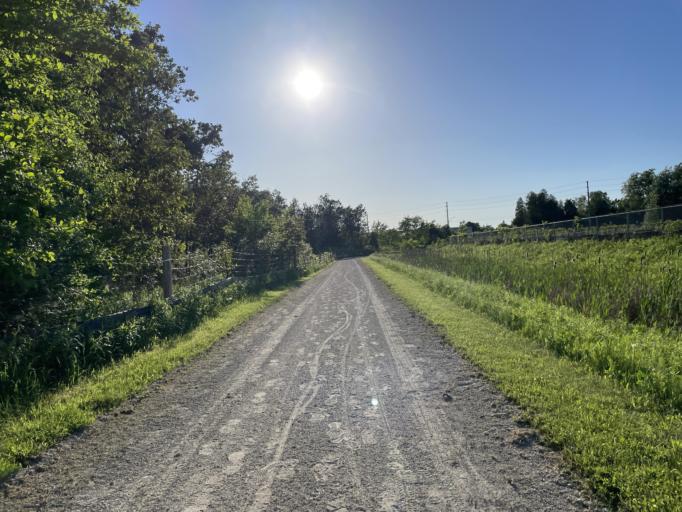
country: CA
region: Ontario
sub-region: Wellington County
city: Guelph
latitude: 43.4929
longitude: -80.2254
